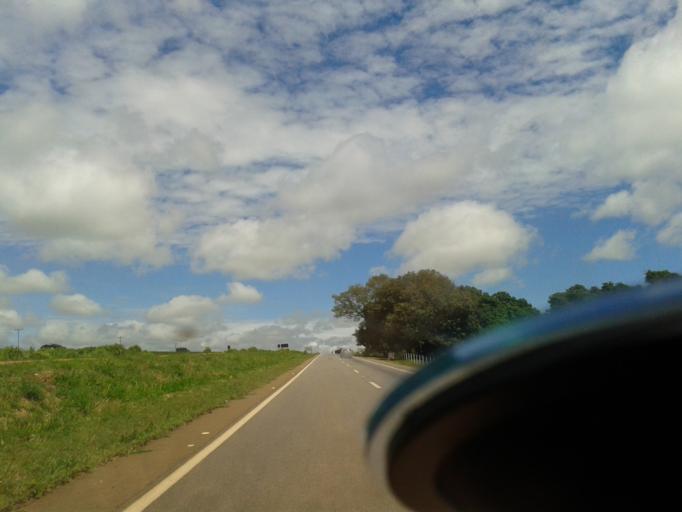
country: BR
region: Goias
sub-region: Inhumas
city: Inhumas
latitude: -16.2579
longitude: -49.5501
